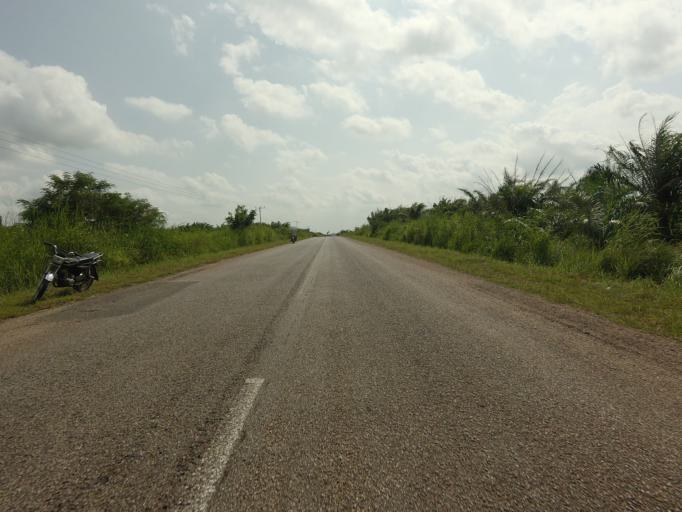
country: TG
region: Maritime
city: Tsevie
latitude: 6.3922
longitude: 0.8260
